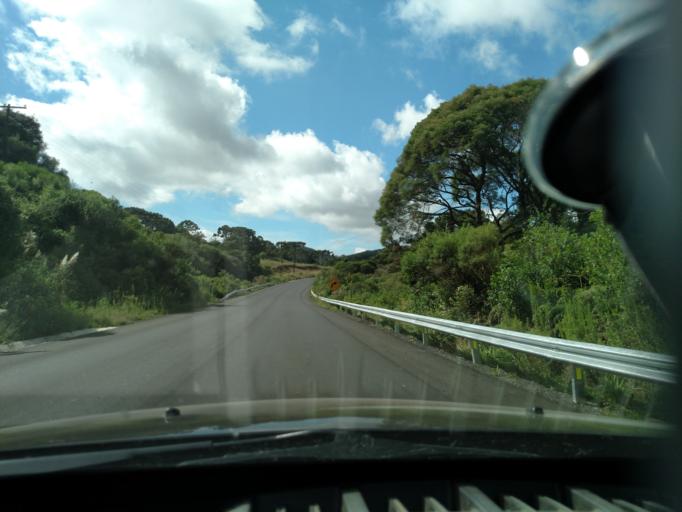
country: BR
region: Santa Catarina
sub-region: Lages
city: Lages
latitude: -27.9320
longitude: -50.0969
